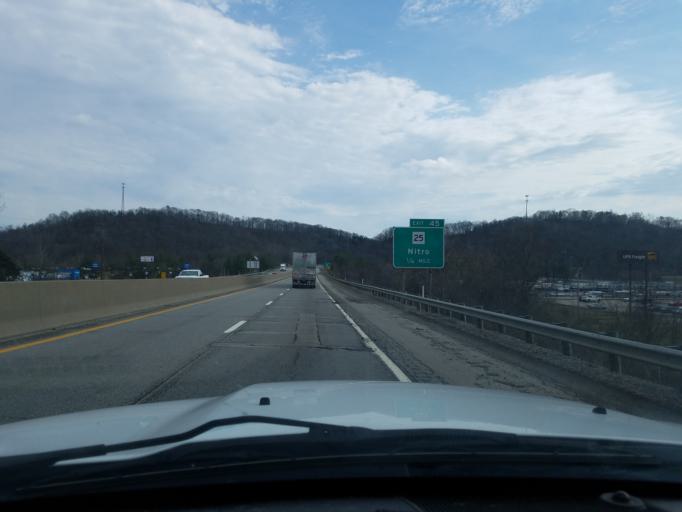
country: US
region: West Virginia
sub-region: Kanawha County
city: Nitro
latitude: 38.4425
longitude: -81.8368
